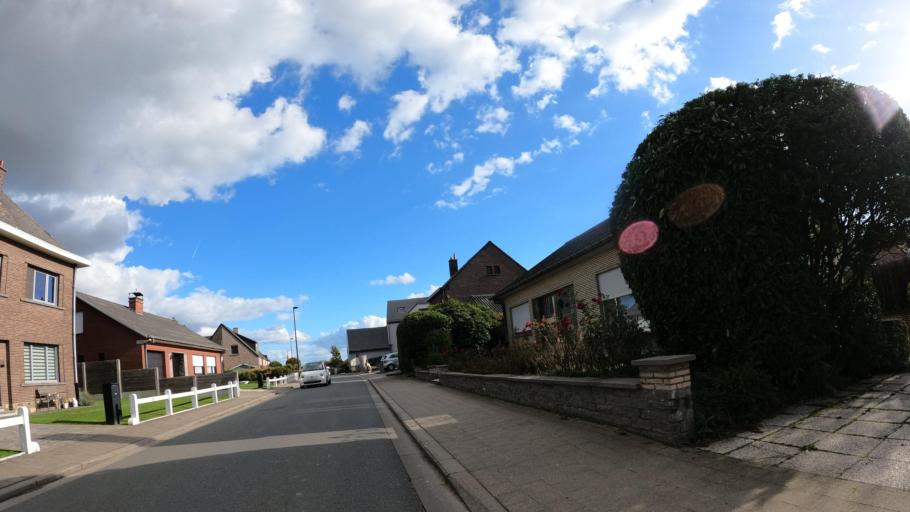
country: BE
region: Flanders
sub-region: Provincie Vlaams-Brabant
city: Asse
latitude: 50.9205
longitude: 4.1883
